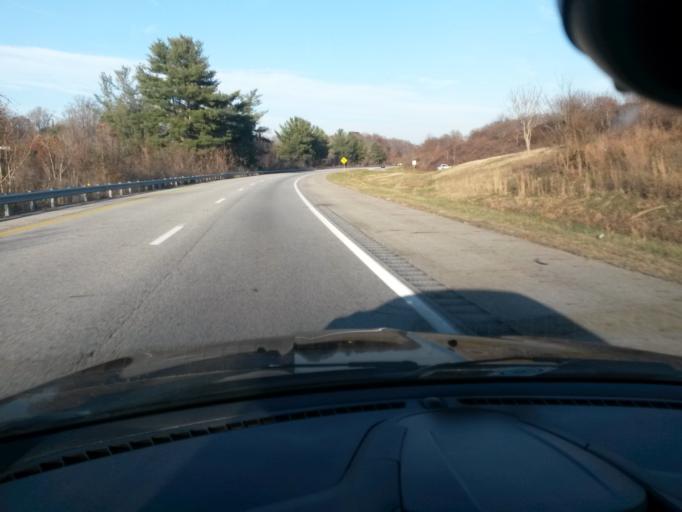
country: US
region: Virginia
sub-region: Amherst County
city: Amherst
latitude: 37.5624
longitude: -79.0630
